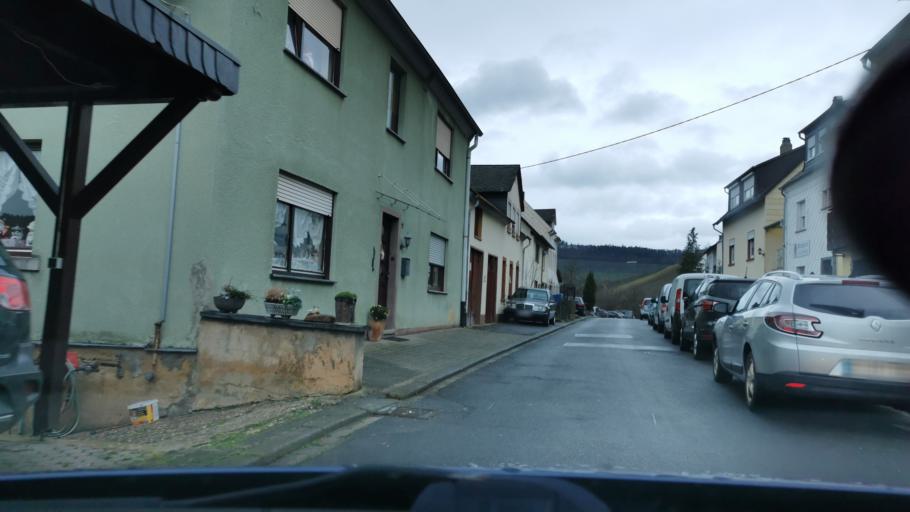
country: DE
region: Rheinland-Pfalz
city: Maring-Noviand
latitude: 49.9277
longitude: 7.0010
